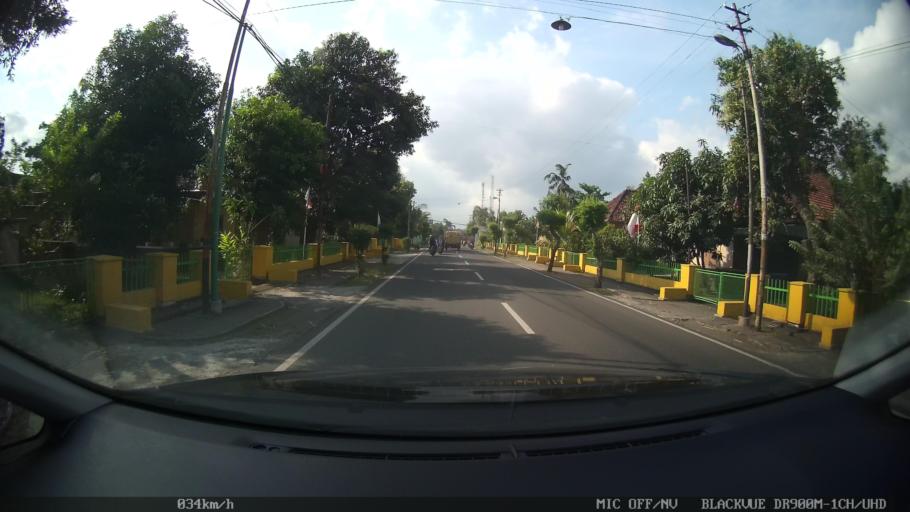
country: ID
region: Daerah Istimewa Yogyakarta
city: Kasihan
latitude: -7.8301
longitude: 110.3443
